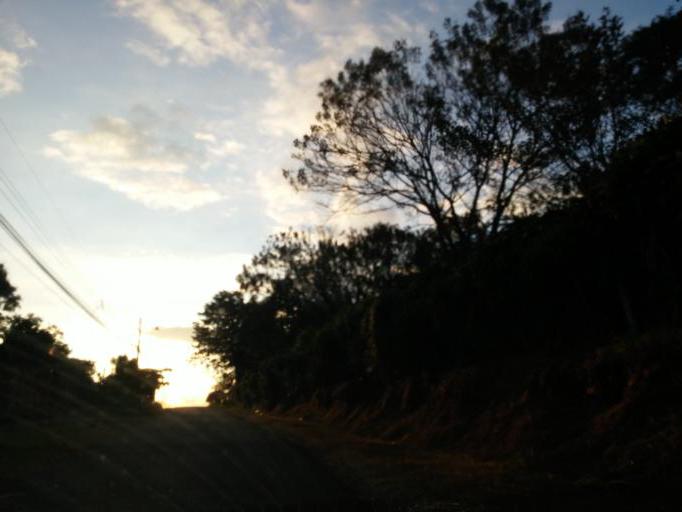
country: CR
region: Alajuela
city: Alajuela
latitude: 10.0390
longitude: -84.2082
